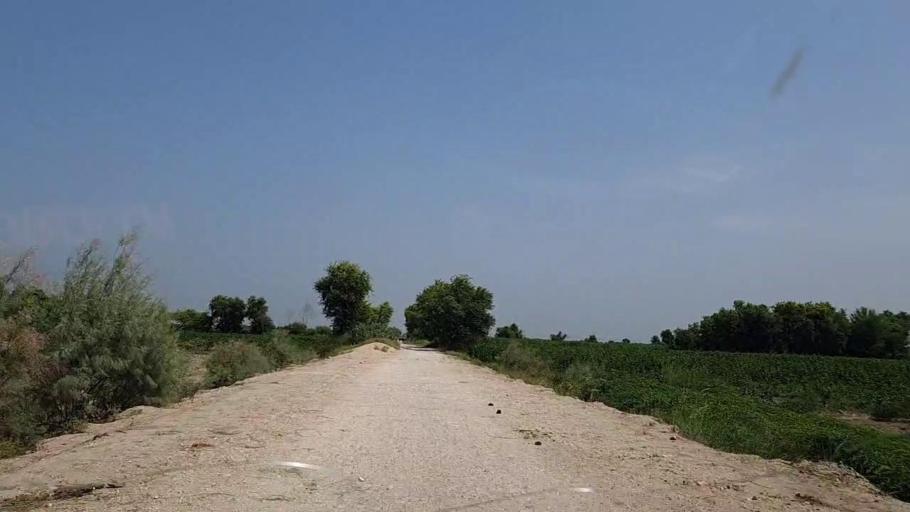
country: PK
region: Sindh
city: Adilpur
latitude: 27.8405
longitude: 69.2763
